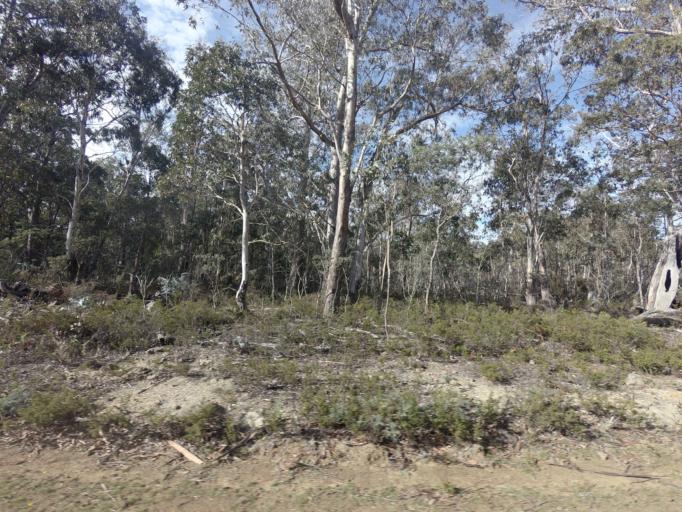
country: AU
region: Tasmania
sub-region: Sorell
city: Sorell
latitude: -42.5134
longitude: 147.4751
